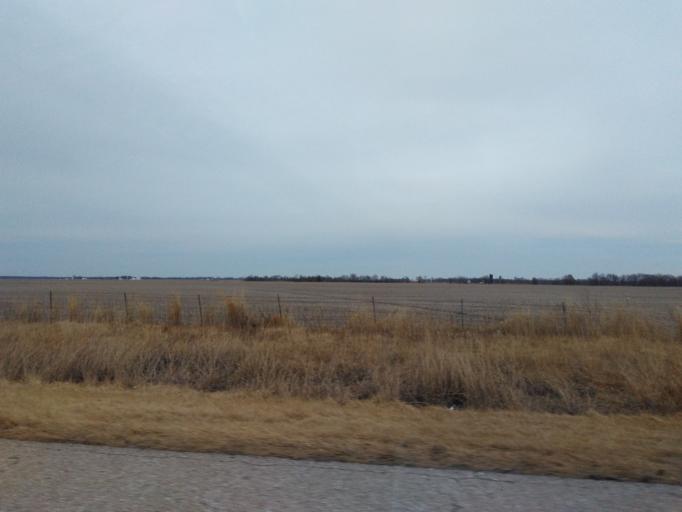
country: US
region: Illinois
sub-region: Washington County
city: Okawville
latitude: 38.4218
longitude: -89.4524
